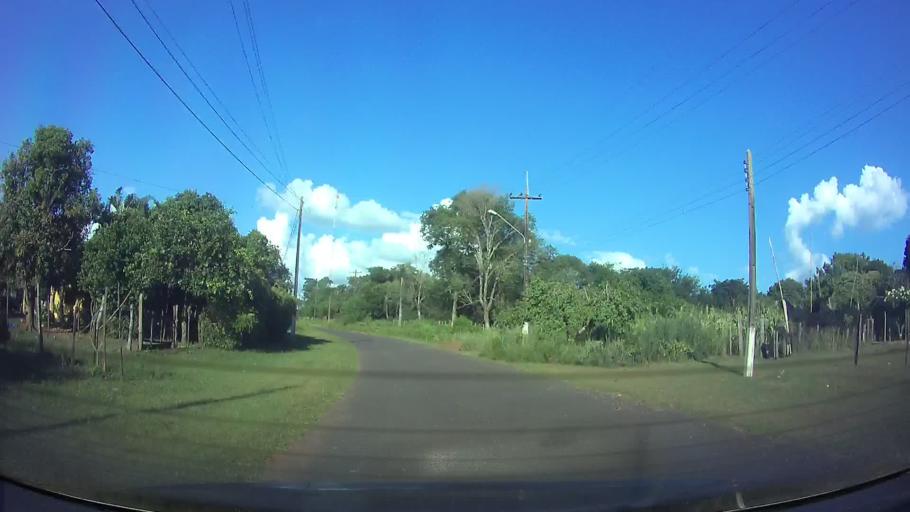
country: PY
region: Central
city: Aregua
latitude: -25.3339
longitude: -57.3798
